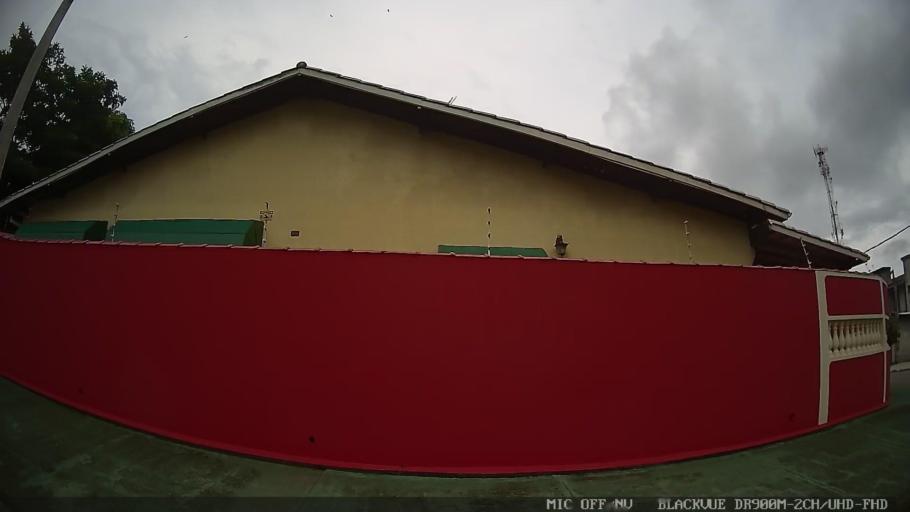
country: BR
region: Sao Paulo
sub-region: Caraguatatuba
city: Caraguatatuba
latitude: -23.6190
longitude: -45.3870
